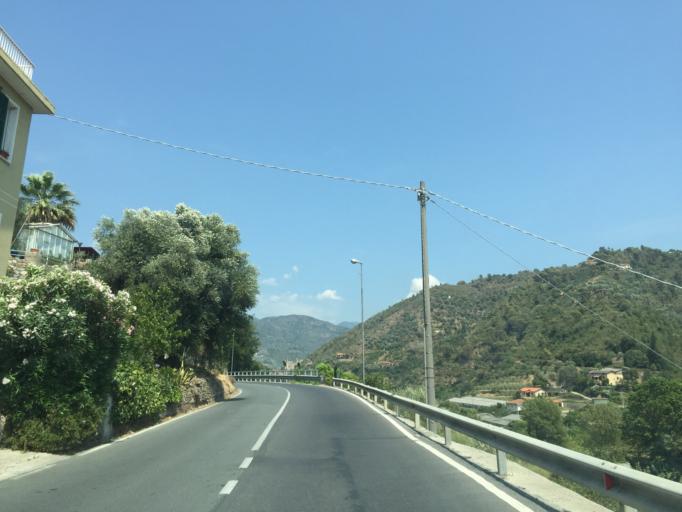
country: IT
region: Liguria
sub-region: Provincia di Imperia
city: Dolceacqua
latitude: 43.8386
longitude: 7.6268
